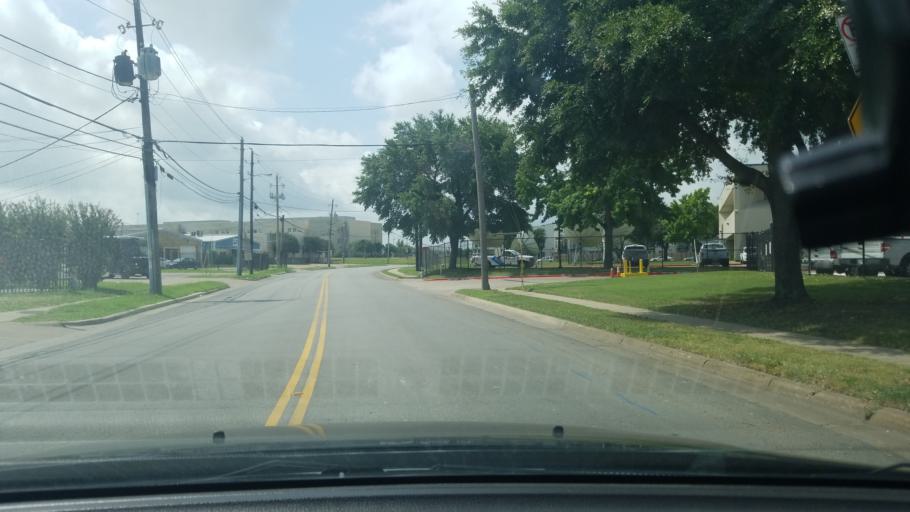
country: US
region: Texas
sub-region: Dallas County
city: Mesquite
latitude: 32.8041
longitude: -96.6888
